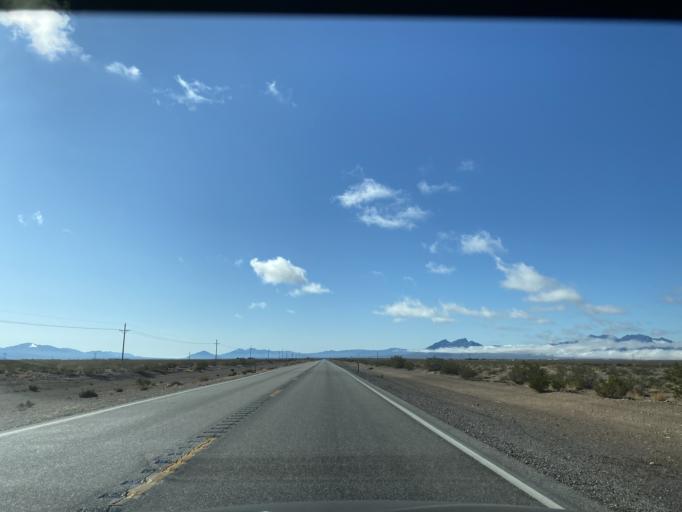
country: US
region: Nevada
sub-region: Nye County
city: Beatty
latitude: 36.5490
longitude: -116.4169
